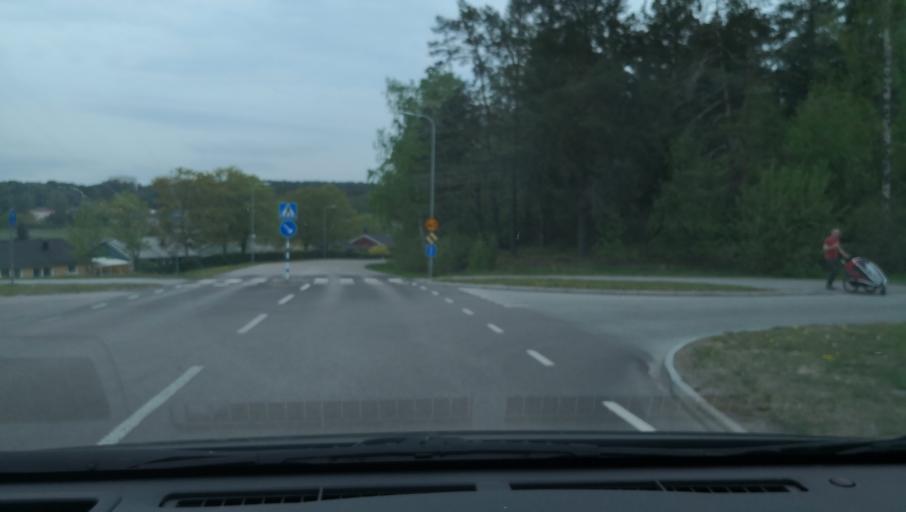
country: SE
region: Stockholm
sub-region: Upplands-Bro Kommun
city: Kungsaengen
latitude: 59.4913
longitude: 17.7382
